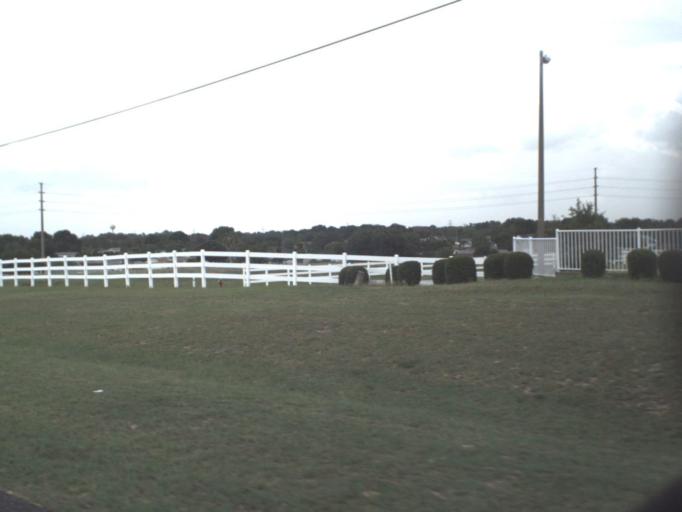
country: US
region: Florida
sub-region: Sumter County
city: The Villages
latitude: 28.9717
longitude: -81.9773
